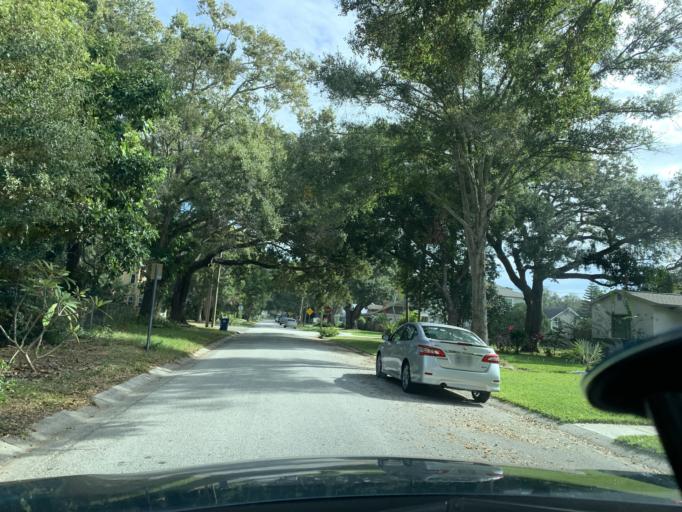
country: US
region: Florida
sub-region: Pinellas County
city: Saint Petersburg
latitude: 27.7929
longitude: -82.6576
